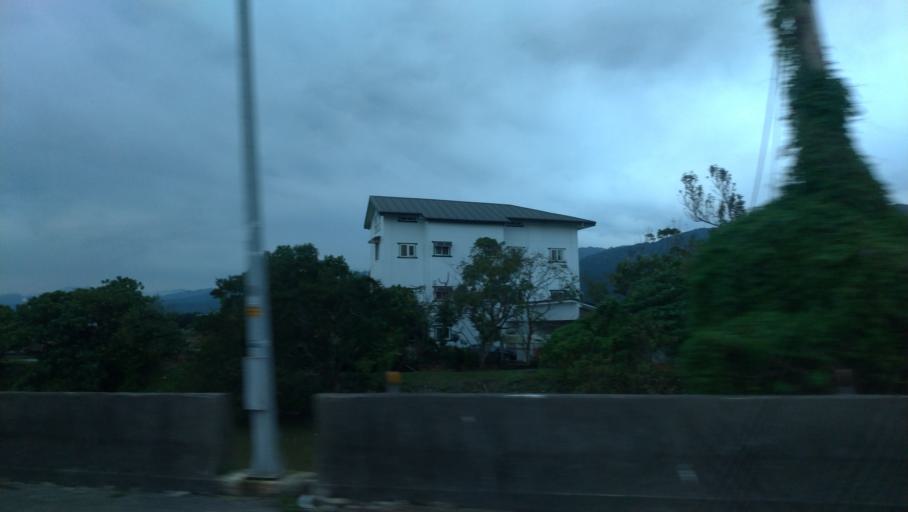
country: TW
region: Taiwan
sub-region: Yilan
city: Yilan
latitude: 24.8285
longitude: 121.8016
